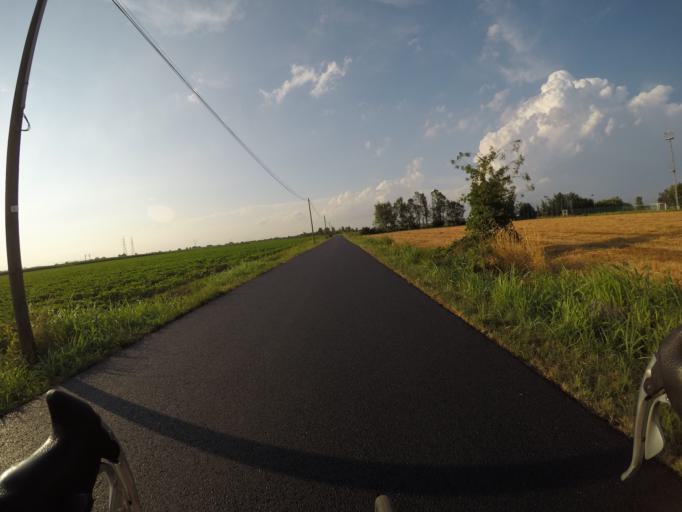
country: IT
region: Veneto
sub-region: Provincia di Rovigo
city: San Bellino
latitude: 45.0314
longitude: 11.5858
